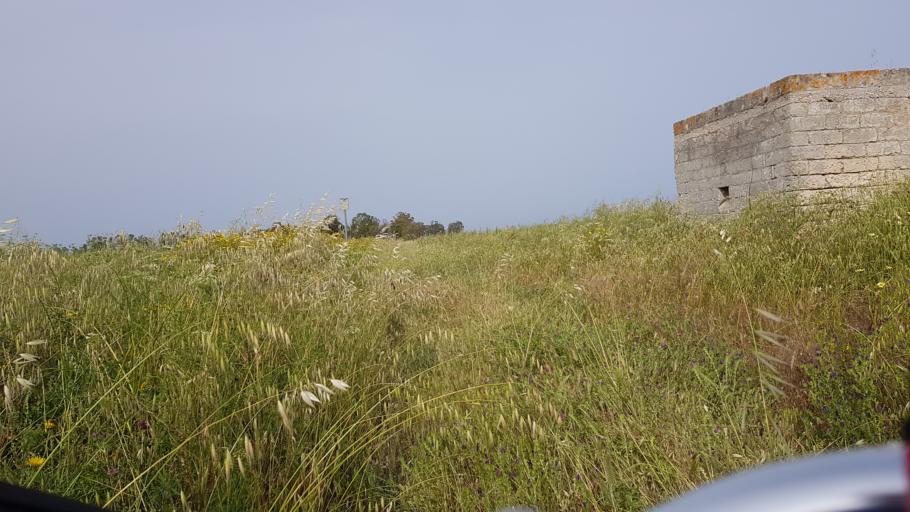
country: IT
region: Apulia
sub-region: Provincia di Brindisi
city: La Rosa
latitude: 40.5796
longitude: 18.0332
